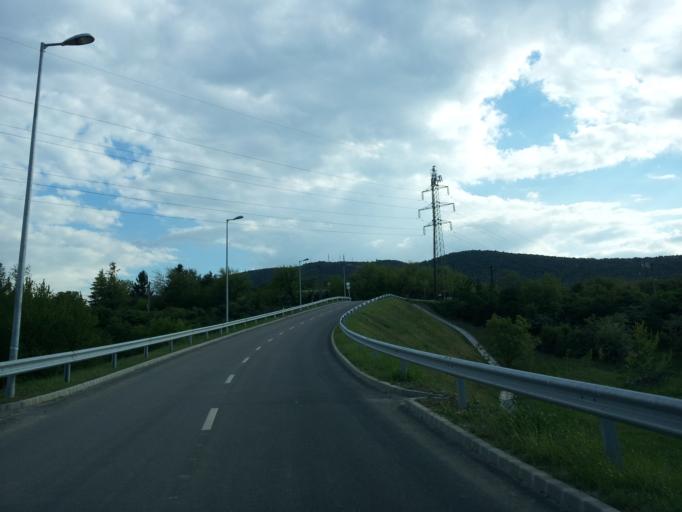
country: HU
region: Pest
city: Urom
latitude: 47.5758
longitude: 19.0082
